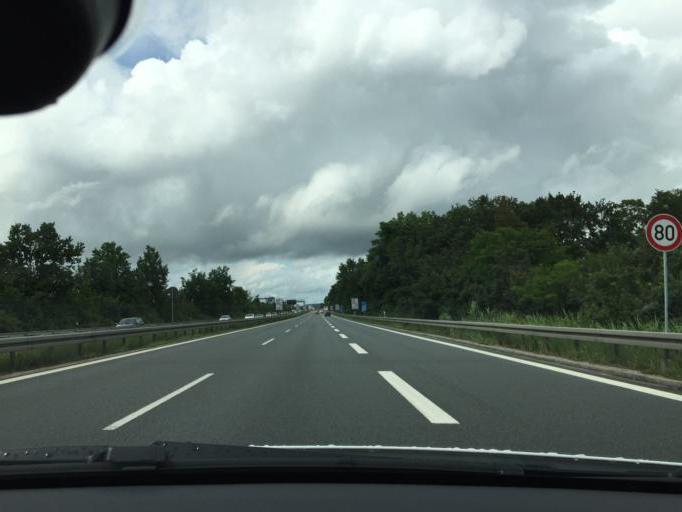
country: DE
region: Bavaria
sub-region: Regierungsbezirk Mittelfranken
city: Erlangen
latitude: 49.5999
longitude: 10.9984
